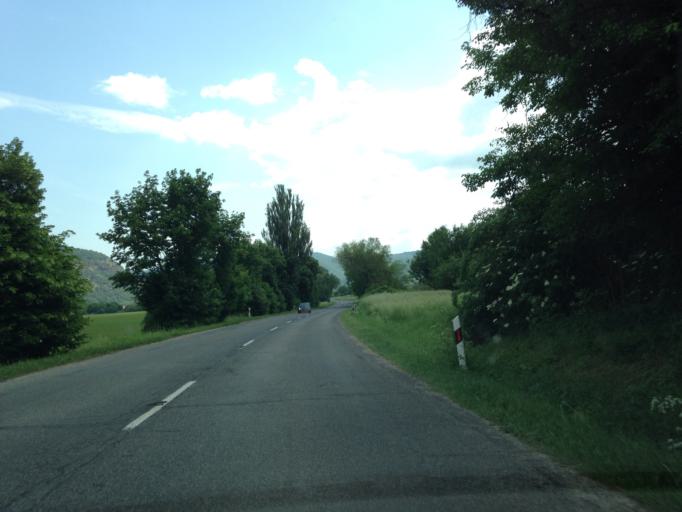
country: HU
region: Komarom-Esztergom
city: Pilismarot
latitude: 47.7785
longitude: 18.8902
